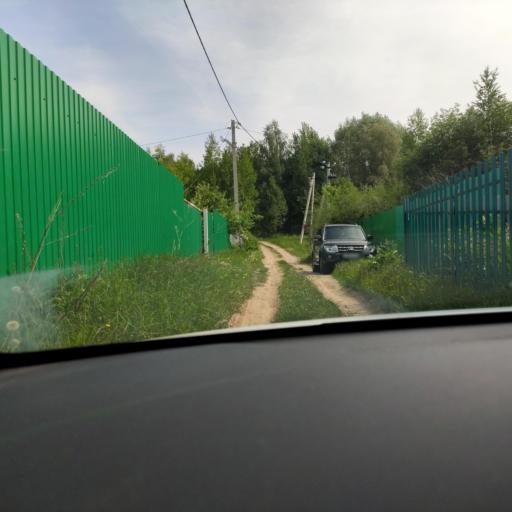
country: RU
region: Tatarstan
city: Vysokaya Gora
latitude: 55.9930
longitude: 49.3266
